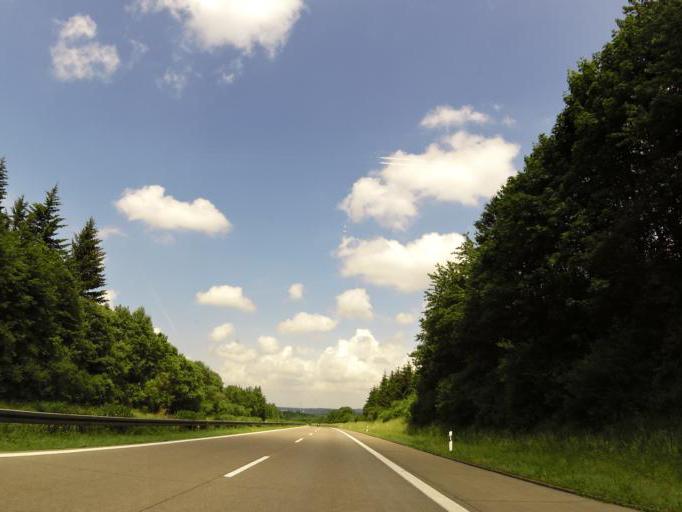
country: DE
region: Baden-Wuerttemberg
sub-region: Regierungsbezirk Stuttgart
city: Nattheim
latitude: 48.7744
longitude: 10.2132
